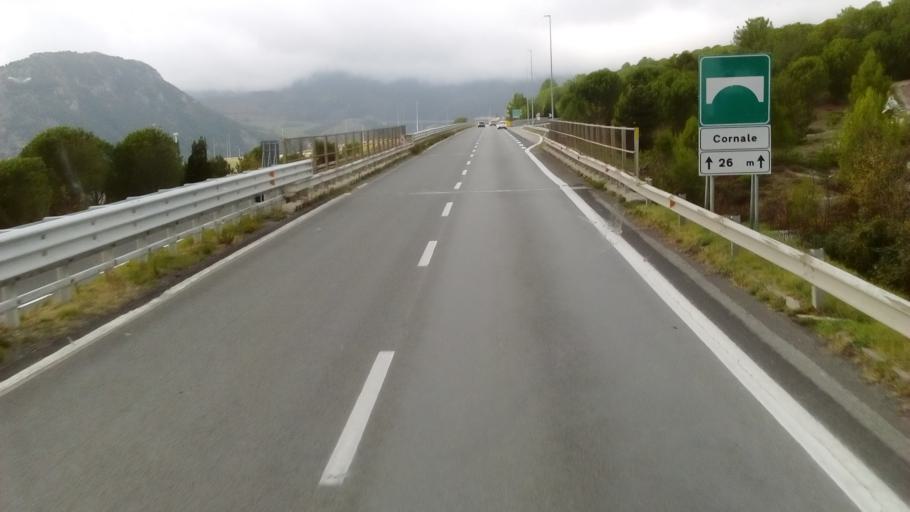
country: IT
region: Calabria
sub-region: Provincia di Cosenza
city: Morano Calabro
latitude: 39.8723
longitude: 16.1721
